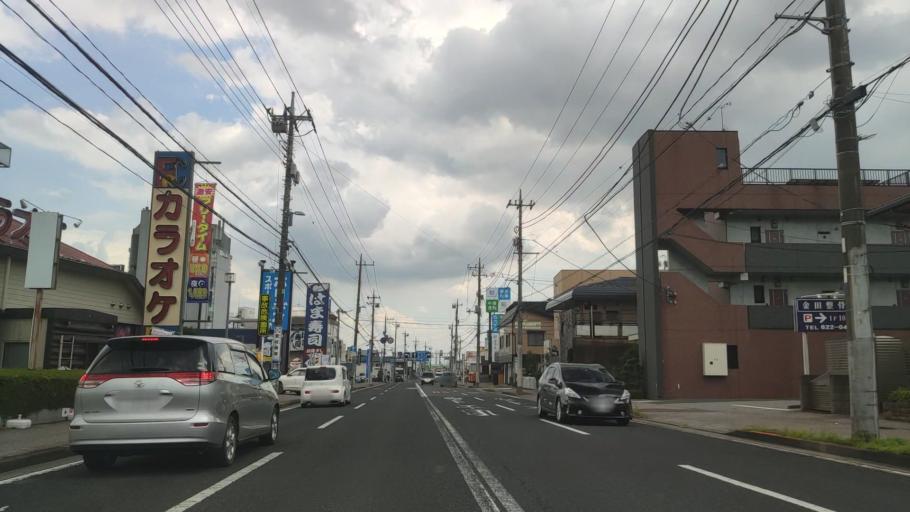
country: JP
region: Tochigi
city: Utsunomiya-shi
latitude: 36.5774
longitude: 139.8705
